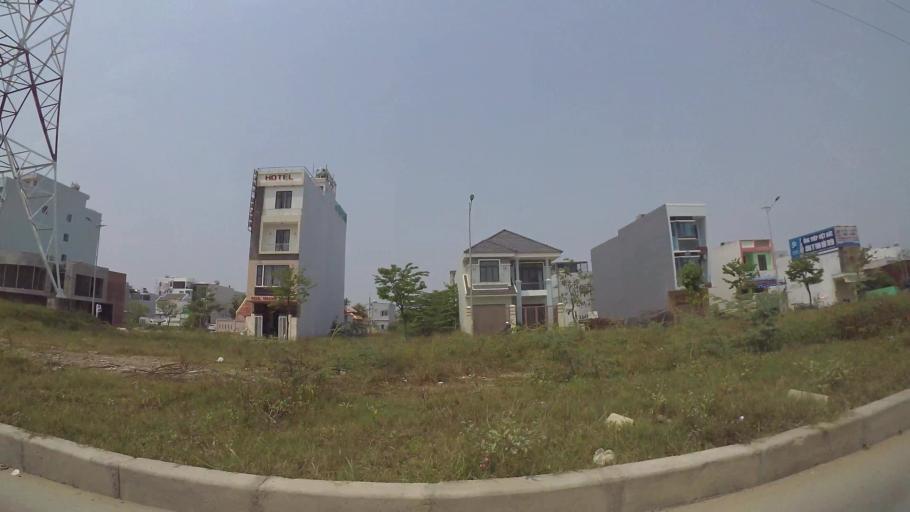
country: VN
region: Da Nang
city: Cam Le
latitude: 16.0101
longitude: 108.2226
